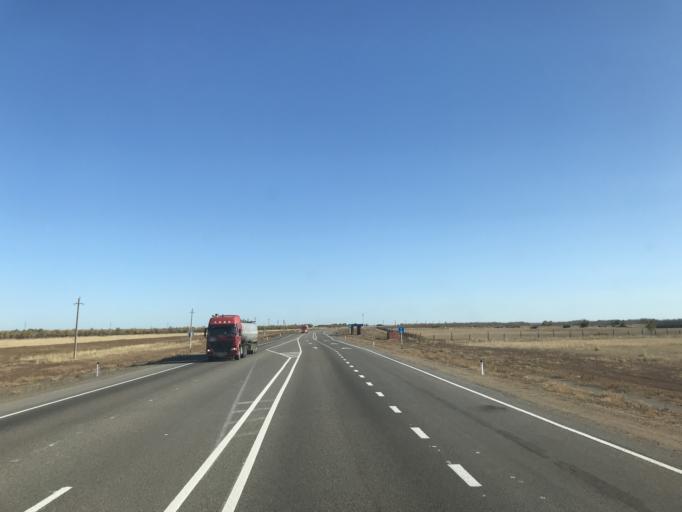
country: KZ
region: Pavlodar
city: Koktobe
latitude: 51.9035
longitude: 77.3778
